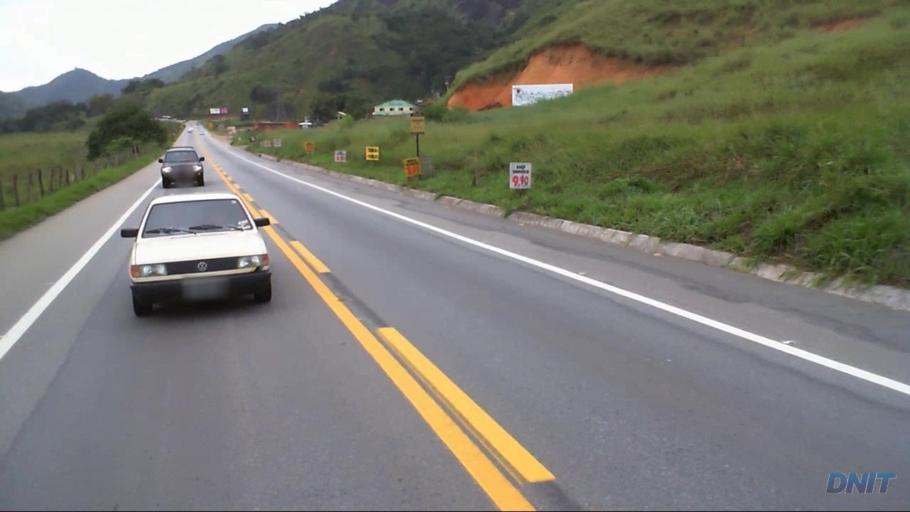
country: BR
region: Minas Gerais
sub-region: Timoteo
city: Timoteo
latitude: -19.5880
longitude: -42.7337
